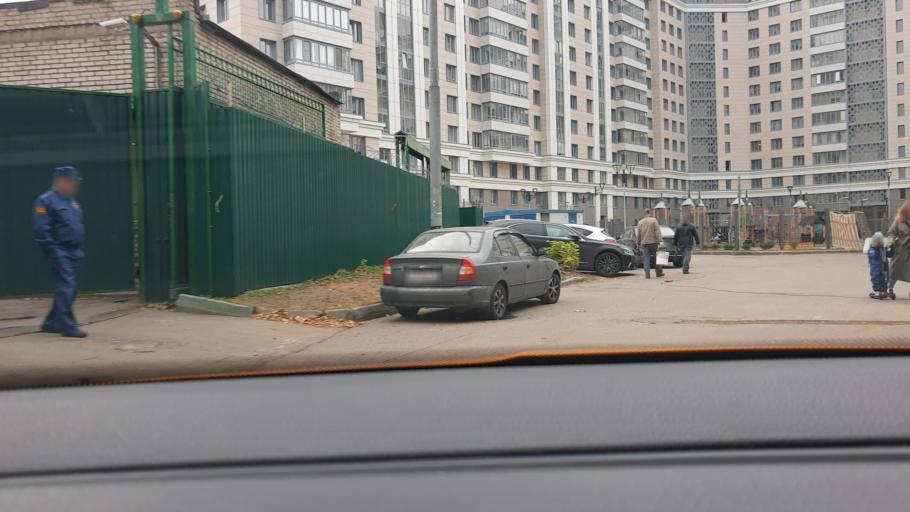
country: RU
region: Moscow
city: Sokol
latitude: 55.7951
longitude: 37.5245
